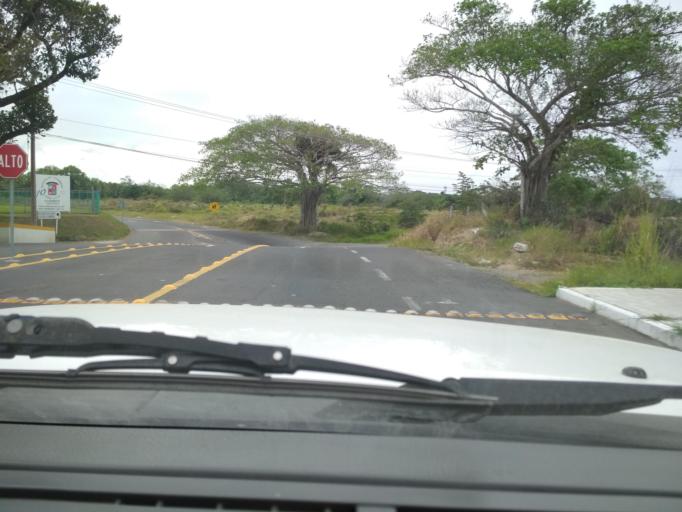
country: MX
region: Veracruz
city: Boca del Rio
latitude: 19.0893
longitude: -96.1201
